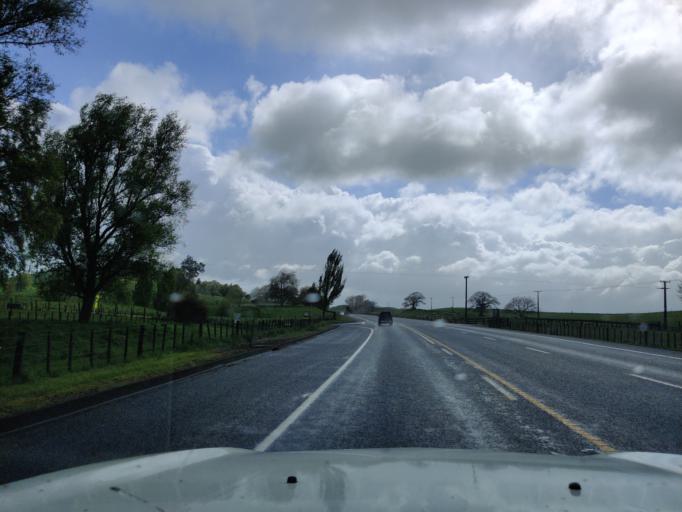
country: NZ
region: Waikato
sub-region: Matamata-Piako District
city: Matamata
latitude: -37.9830
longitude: 175.7342
